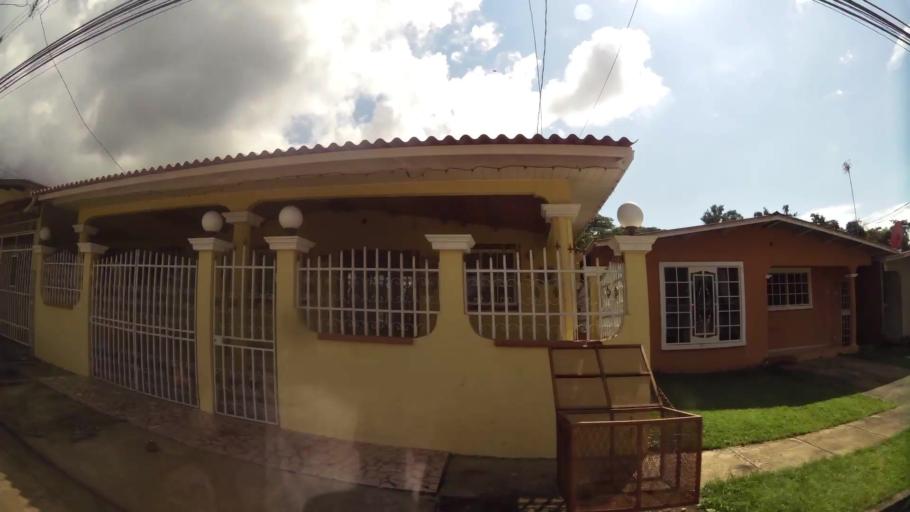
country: PA
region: Panama
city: Nuevo Arraijan
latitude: 8.9145
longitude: -79.7399
